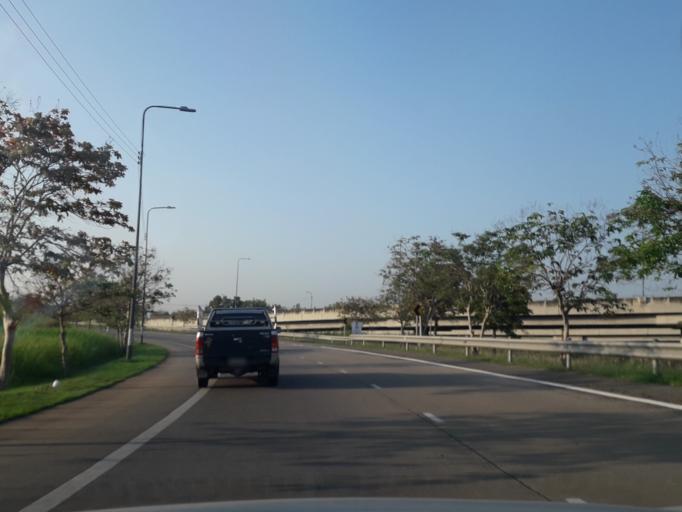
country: TH
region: Phra Nakhon Si Ayutthaya
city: Bang Pa-in
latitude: 14.1487
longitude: 100.5553
